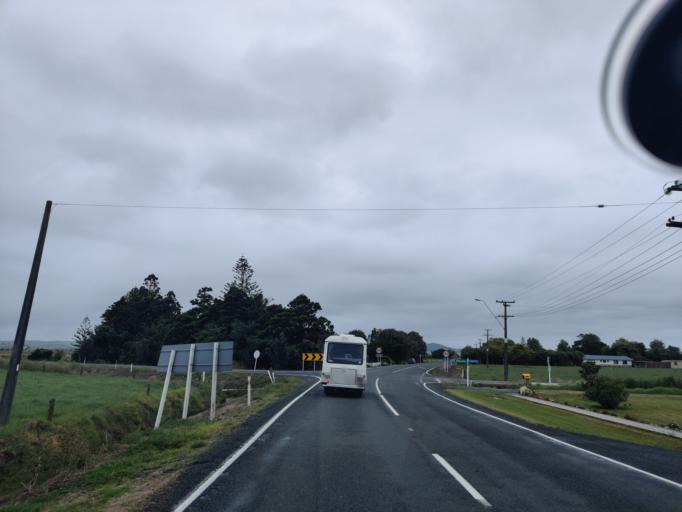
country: NZ
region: Northland
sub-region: Kaipara District
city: Dargaville
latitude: -36.1289
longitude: 174.0355
